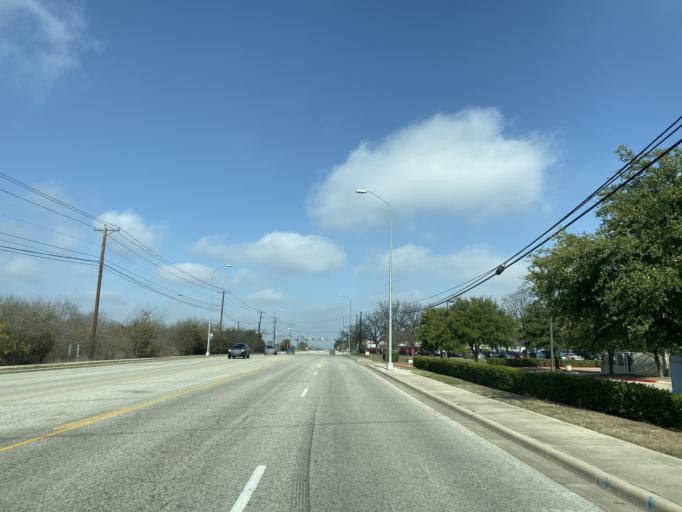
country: US
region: Texas
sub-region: Williamson County
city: Round Rock
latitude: 30.5339
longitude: -97.6950
